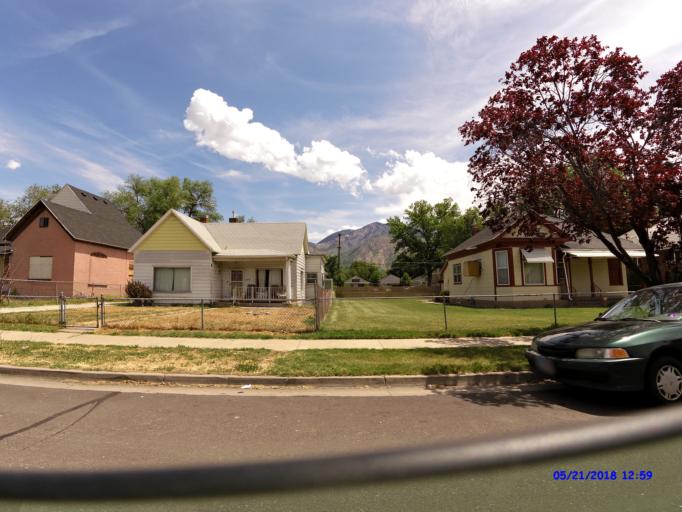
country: US
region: Utah
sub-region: Weber County
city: Ogden
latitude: 41.2133
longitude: -111.9763
